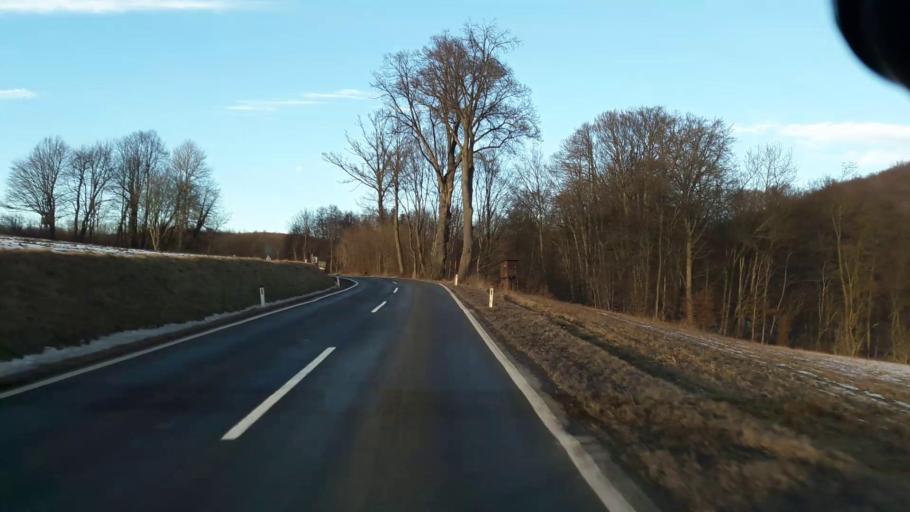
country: AT
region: Lower Austria
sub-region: Politischer Bezirk Wien-Umgebung
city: Mauerbach
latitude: 48.2644
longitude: 16.1698
